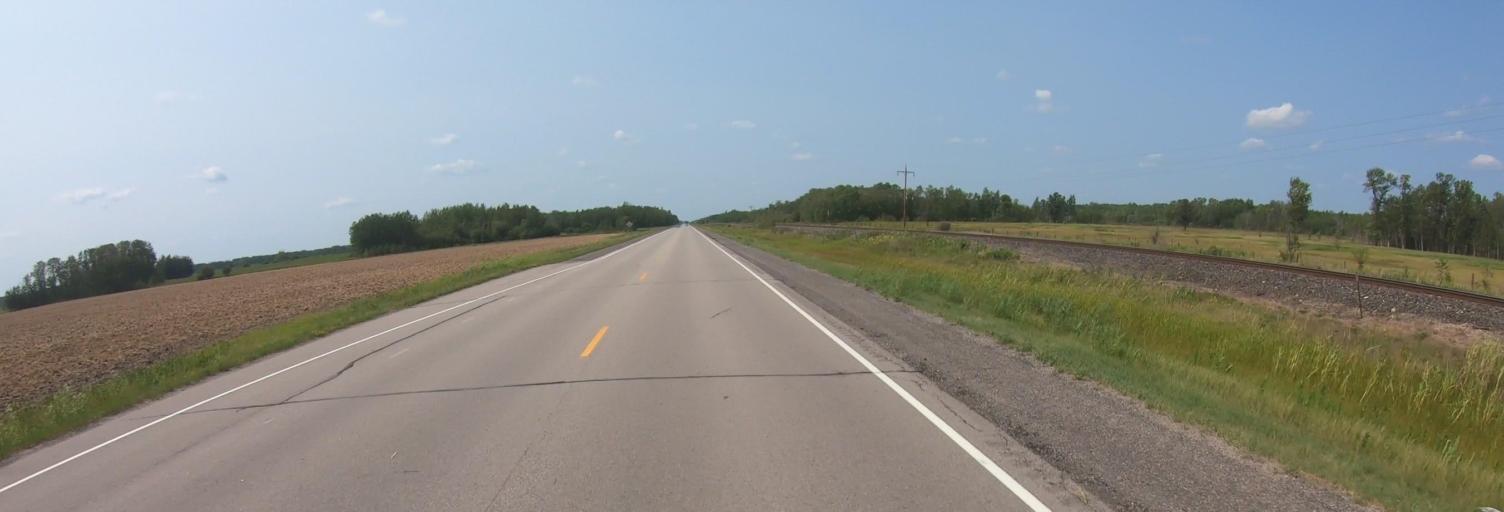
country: US
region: Minnesota
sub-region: Lake of the Woods County
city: Baudette
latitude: 48.7229
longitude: -94.7628
